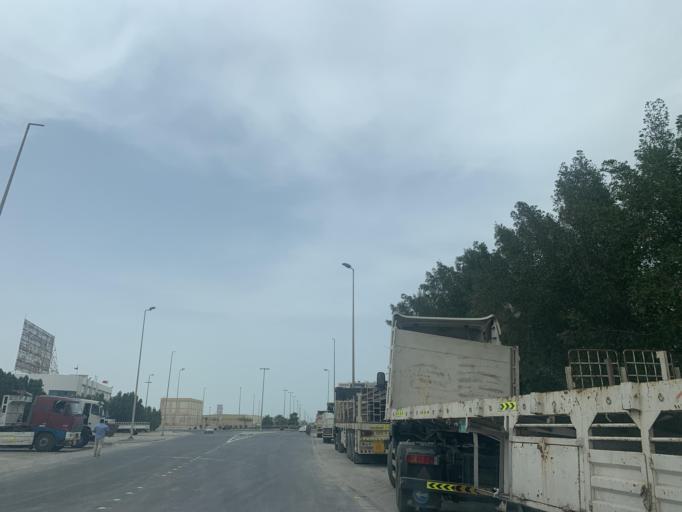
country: BH
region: Muharraq
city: Al Hadd
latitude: 26.2106
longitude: 50.6675
